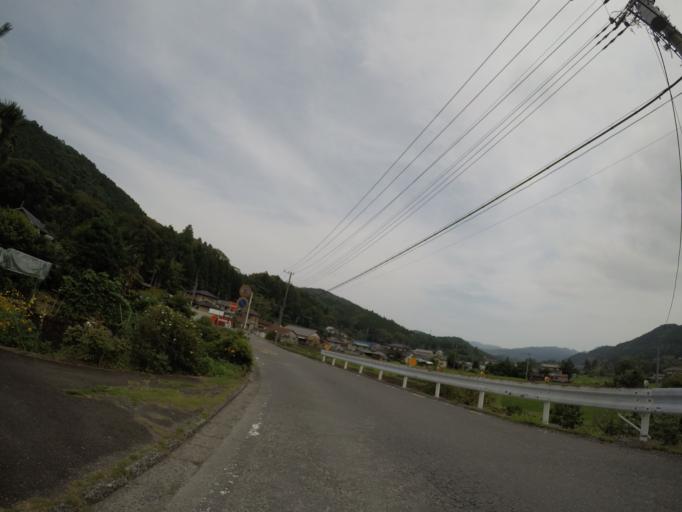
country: JP
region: Shizuoka
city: Fujinomiya
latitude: 35.2246
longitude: 138.5661
